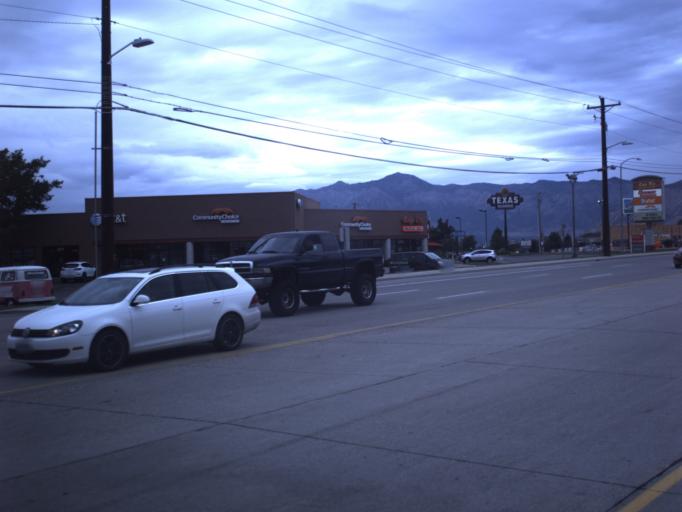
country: US
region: Utah
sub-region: Weber County
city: South Ogden
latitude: 41.1916
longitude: -111.9801
